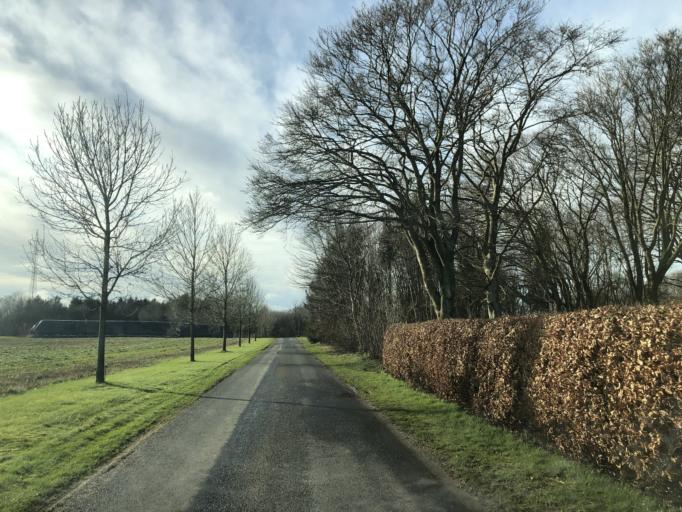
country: DK
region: North Denmark
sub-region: Vesthimmerland Kommune
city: Alestrup
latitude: 56.6405
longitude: 9.6183
